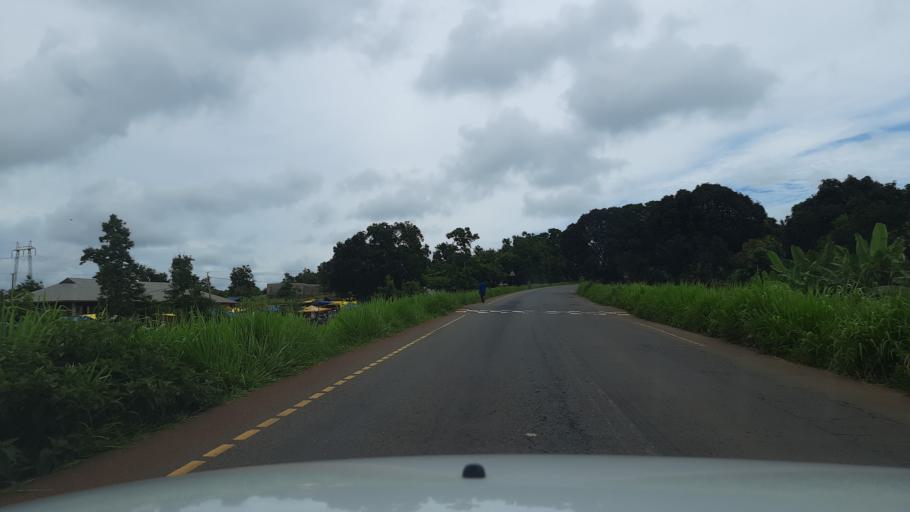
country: TZ
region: Pwani
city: Lugoba
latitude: -6.0856
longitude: 38.2444
